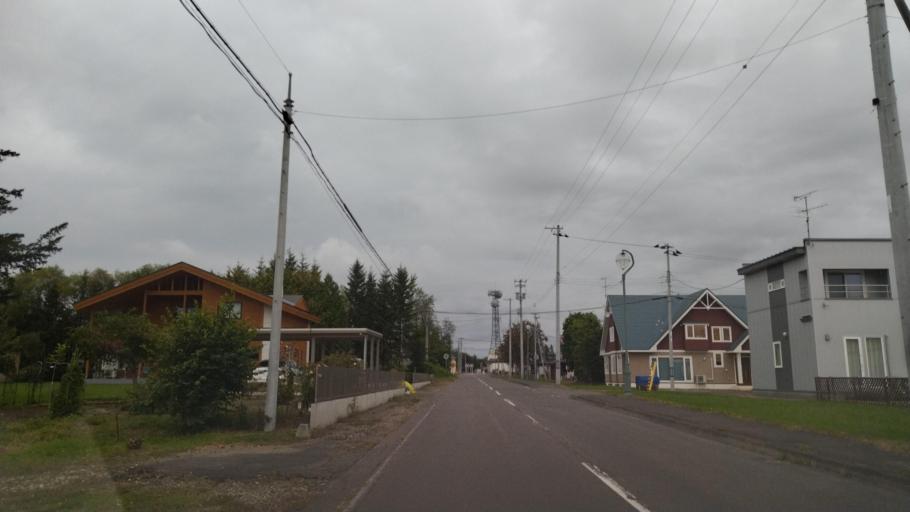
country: JP
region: Hokkaido
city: Otofuke
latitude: 43.2227
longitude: 143.2858
